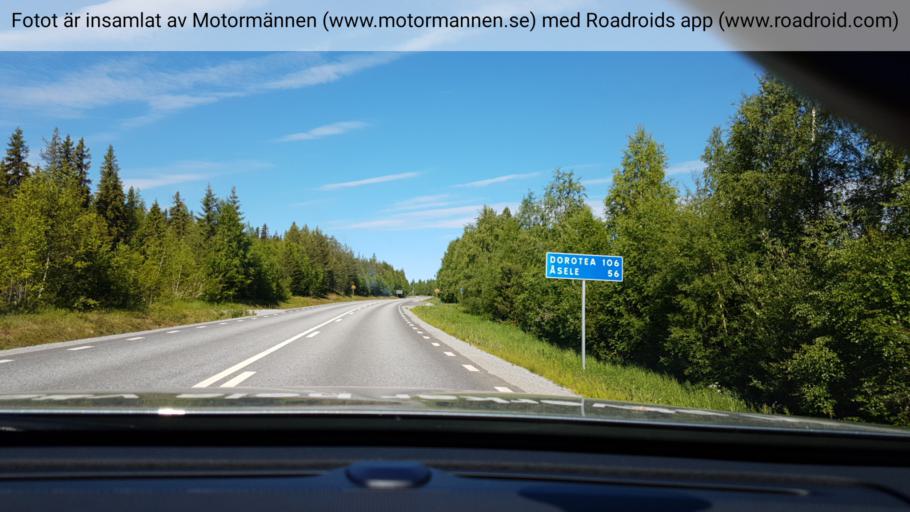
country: SE
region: Vaesterbotten
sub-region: Lycksele Kommun
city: Lycksele
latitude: 64.0693
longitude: 18.3948
